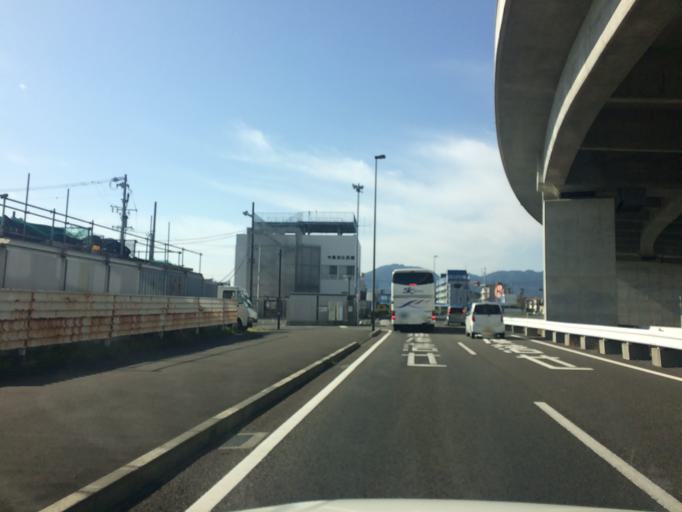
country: JP
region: Shizuoka
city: Shizuoka-shi
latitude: 34.9380
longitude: 138.4003
